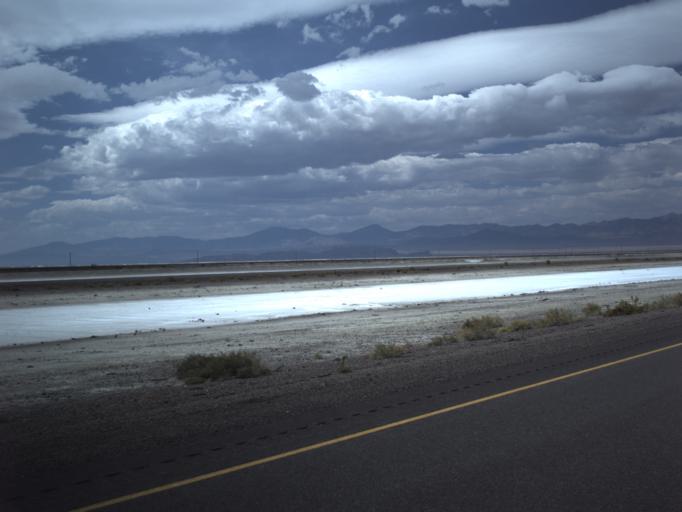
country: US
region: Utah
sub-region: Tooele County
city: Wendover
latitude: 40.7408
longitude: -113.9224
